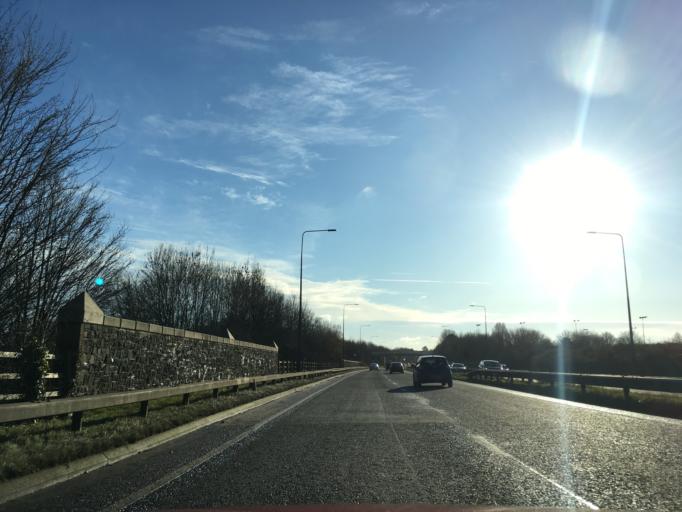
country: GB
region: England
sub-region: South Gloucestershire
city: Kingswood
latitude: 51.4656
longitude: -2.4823
